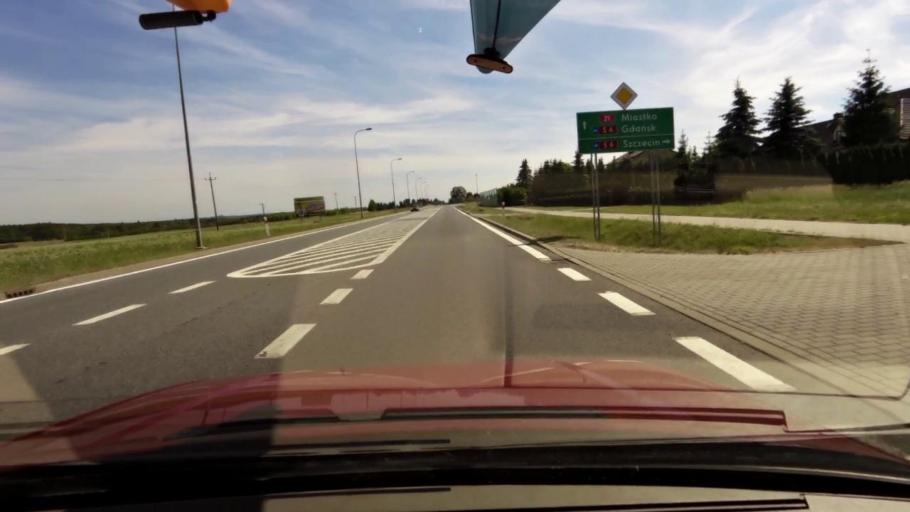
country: PL
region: Pomeranian Voivodeship
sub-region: Powiat slupski
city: Kobylnica
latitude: 54.4276
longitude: 17.0070
